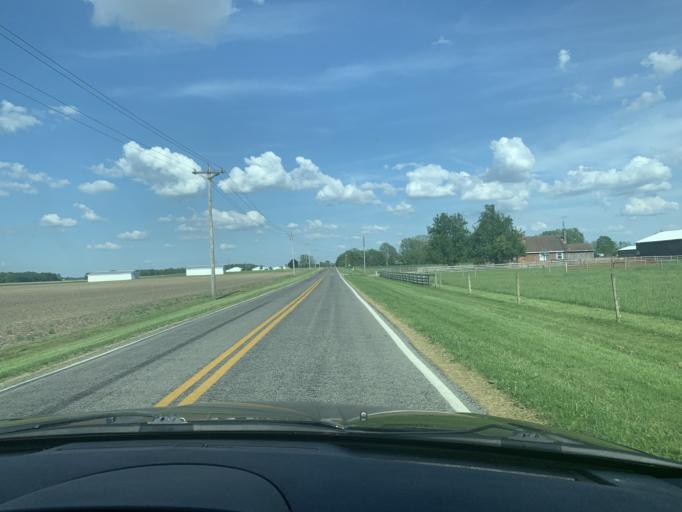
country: US
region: Ohio
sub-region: Logan County
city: De Graff
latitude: 40.2436
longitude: -84.0066
